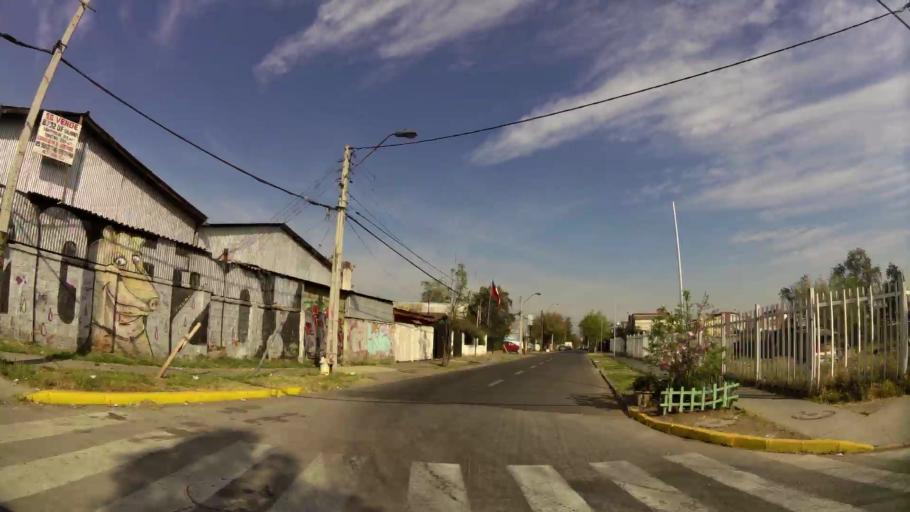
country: CL
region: Santiago Metropolitan
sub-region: Provincia de Santiago
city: Santiago
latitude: -33.5153
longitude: -70.6372
